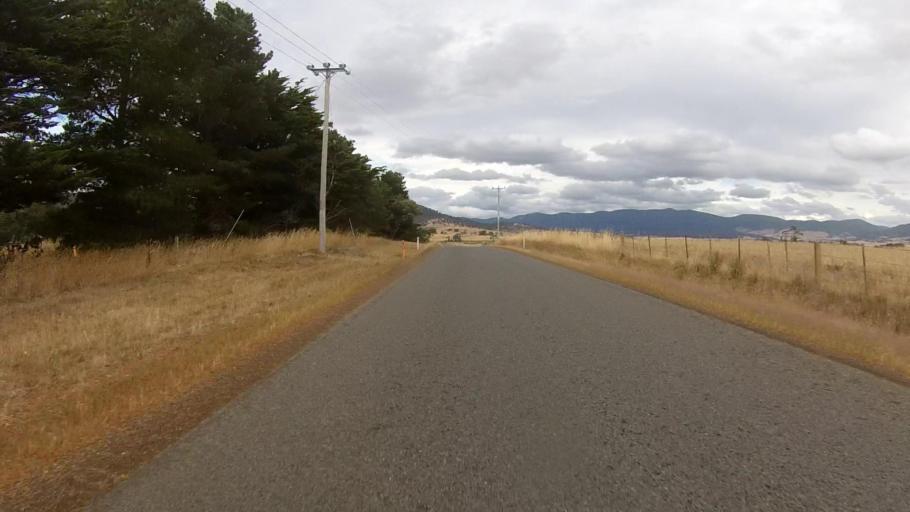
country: AU
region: Tasmania
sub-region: Northern Midlands
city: Evandale
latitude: -41.7864
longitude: 147.7307
